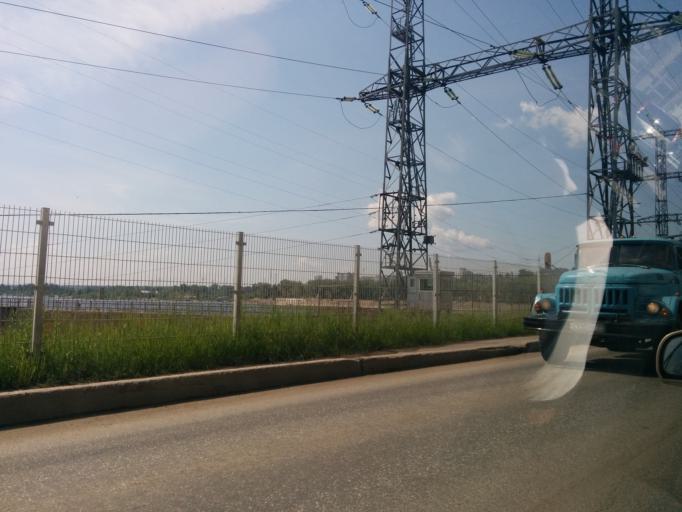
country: RU
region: Perm
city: Perm
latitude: 58.1145
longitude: 56.3327
